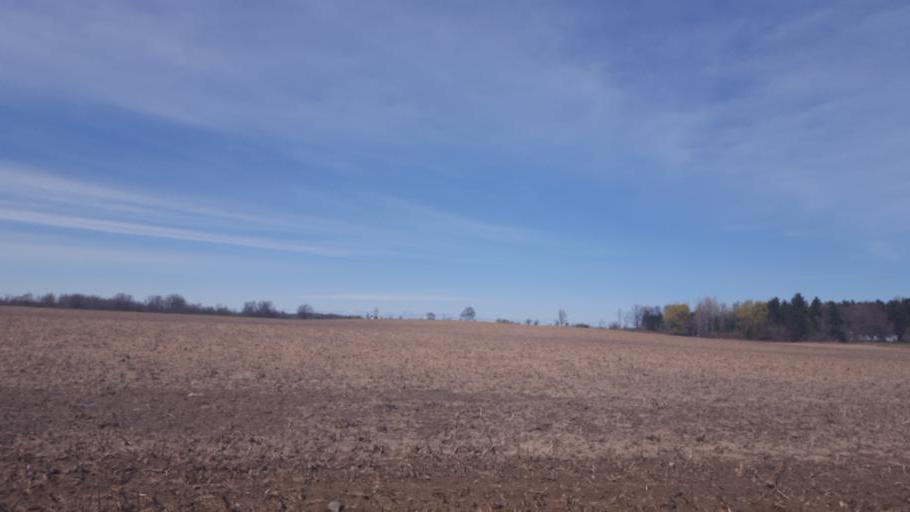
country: US
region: Michigan
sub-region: Gladwin County
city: Gladwin
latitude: 44.0599
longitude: -84.4799
